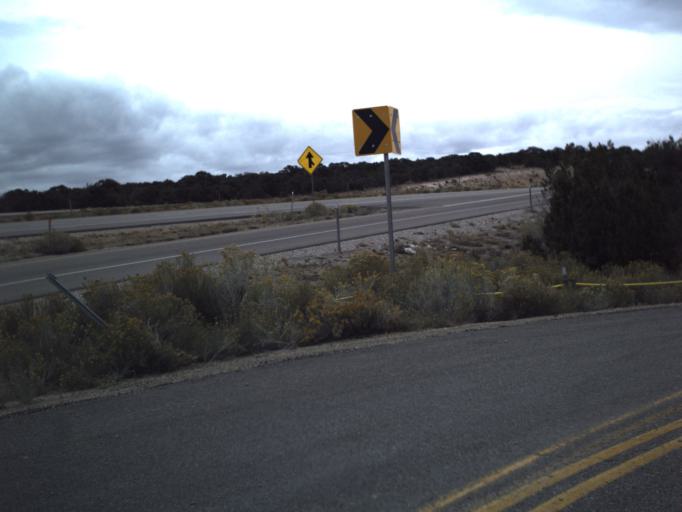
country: US
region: Utah
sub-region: Emery County
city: Ferron
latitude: 38.8538
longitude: -110.9103
